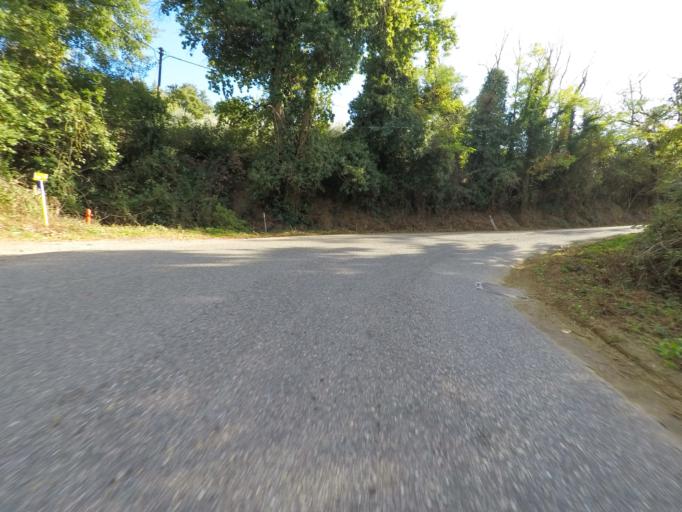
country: IT
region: Tuscany
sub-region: Provincia di Siena
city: Radda in Chianti
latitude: 43.4930
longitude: 11.3885
